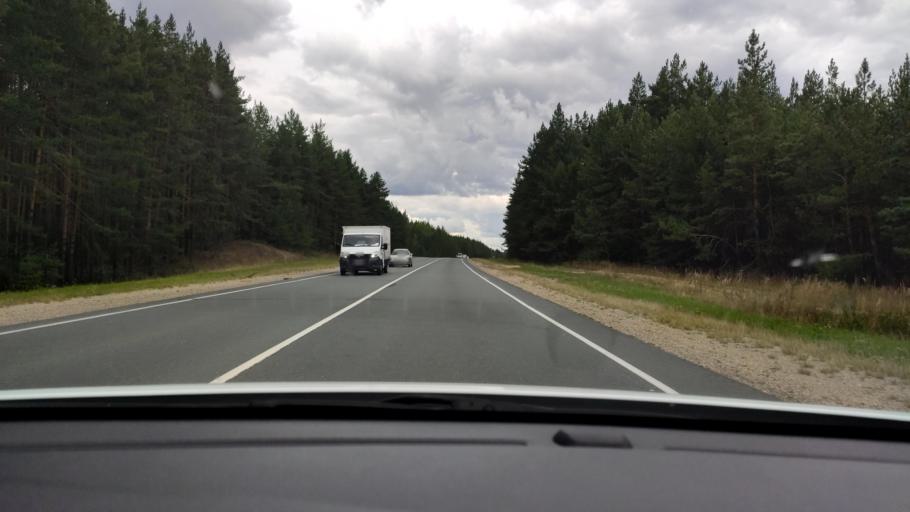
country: RU
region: Mariy-El
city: Krasnogorskiy
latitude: 56.1013
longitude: 48.3438
